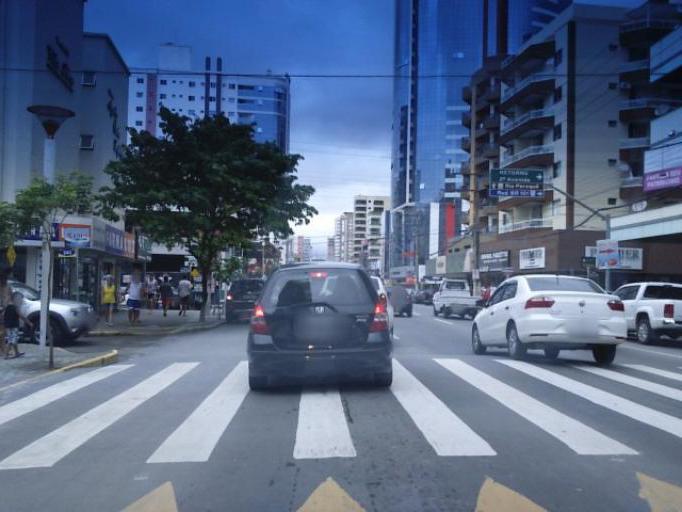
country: BR
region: Santa Catarina
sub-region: Itapema
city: Itapema
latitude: -27.1301
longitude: -48.6005
